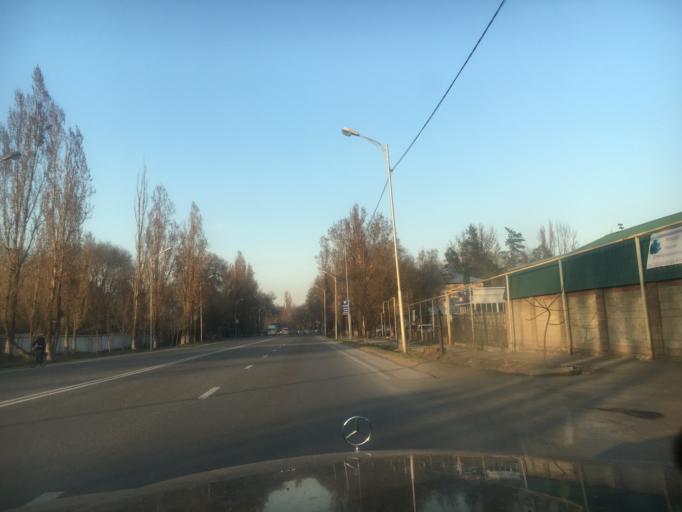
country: KZ
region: Almaty Oblysy
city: Pervomayskiy
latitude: 43.3526
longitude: 76.9740
